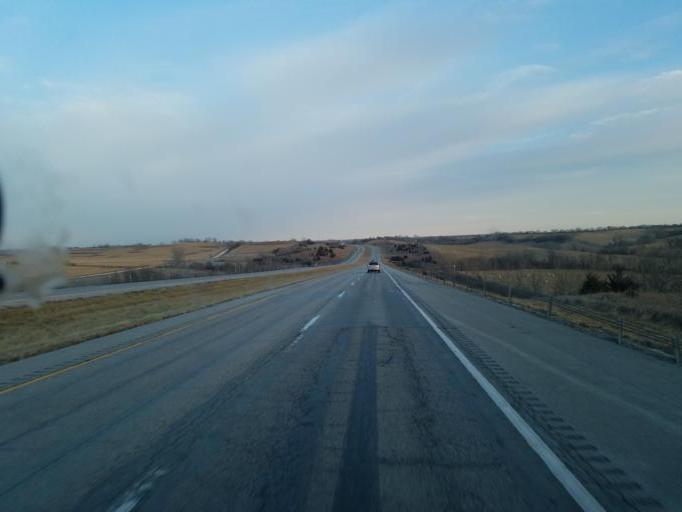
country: US
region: Iowa
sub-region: Harrison County
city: Missouri Valley
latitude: 41.4936
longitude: -95.8320
